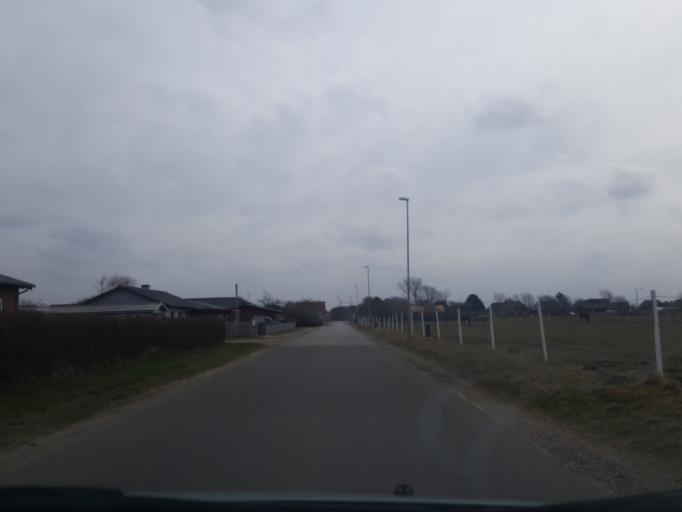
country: DK
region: Central Jutland
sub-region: Ringkobing-Skjern Kommune
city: Ringkobing
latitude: 56.1994
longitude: 8.2097
